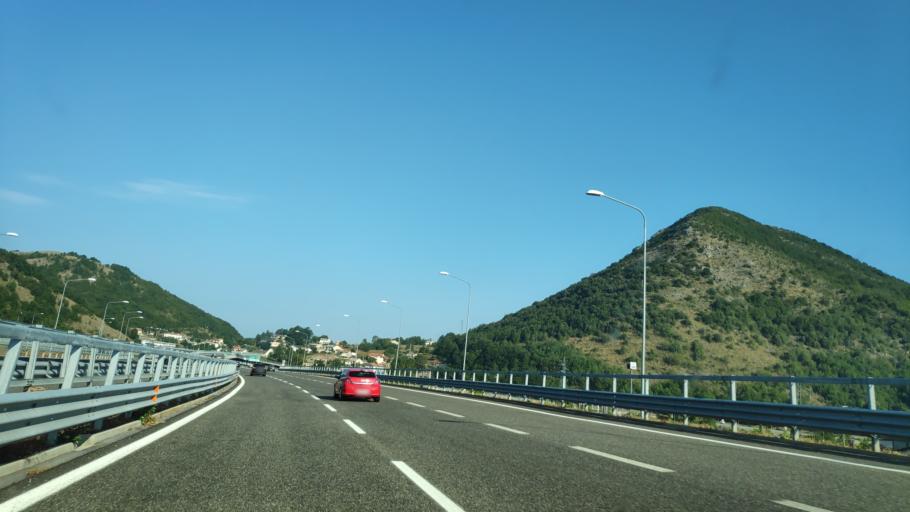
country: IT
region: Basilicate
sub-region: Provincia di Potenza
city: Lauria
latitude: 40.0169
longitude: 15.8917
